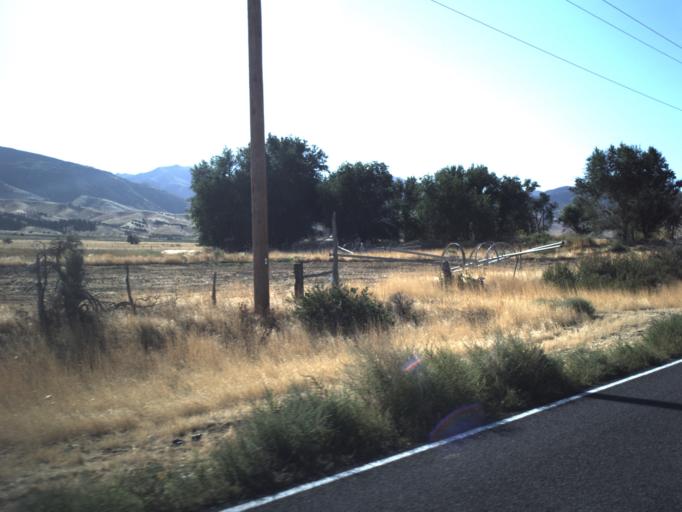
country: US
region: Utah
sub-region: Millard County
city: Delta
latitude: 39.3966
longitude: -112.3355
